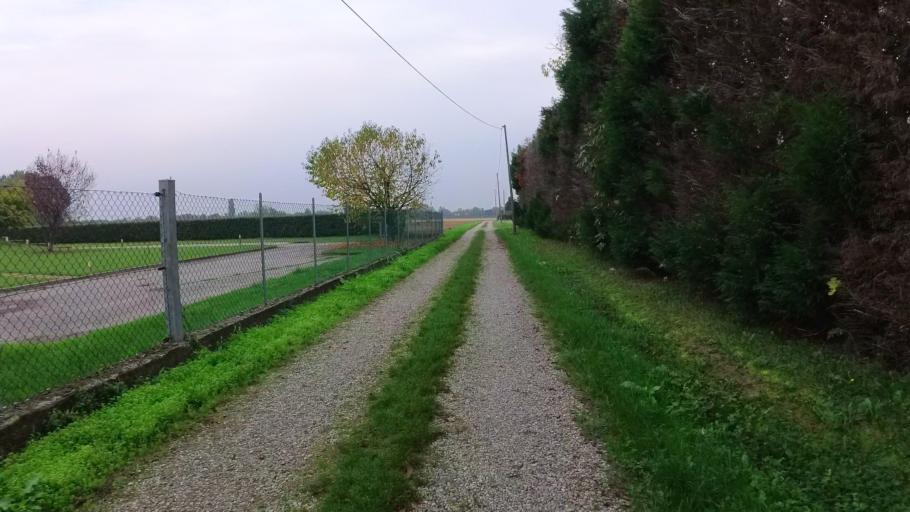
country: IT
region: Veneto
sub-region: Provincia di Padova
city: Bosco
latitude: 45.4385
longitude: 11.7943
